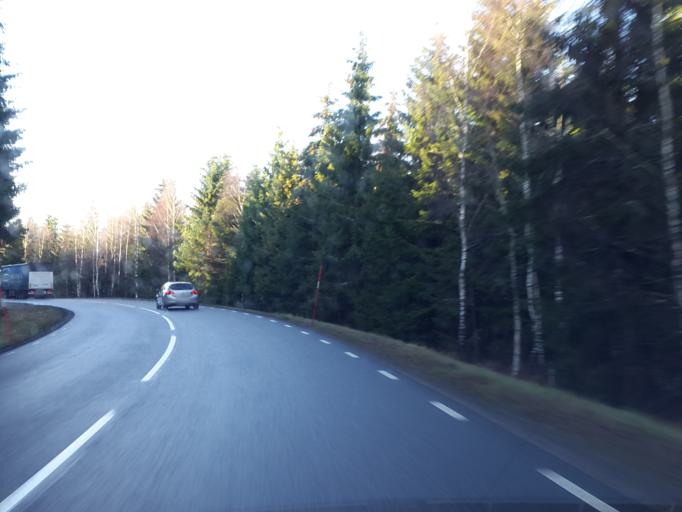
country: SE
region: Vaestra Goetaland
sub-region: Vargarda Kommun
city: Vargarda
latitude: 57.9898
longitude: 12.8314
